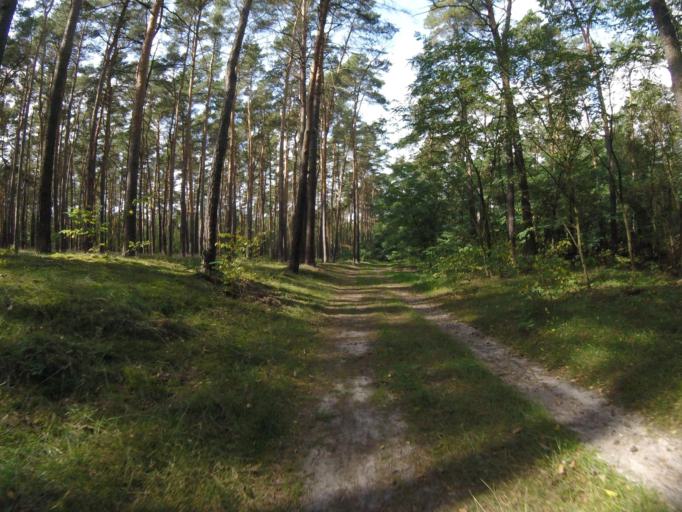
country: DE
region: Brandenburg
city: Mittenwalde
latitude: 52.2344
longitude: 13.5872
